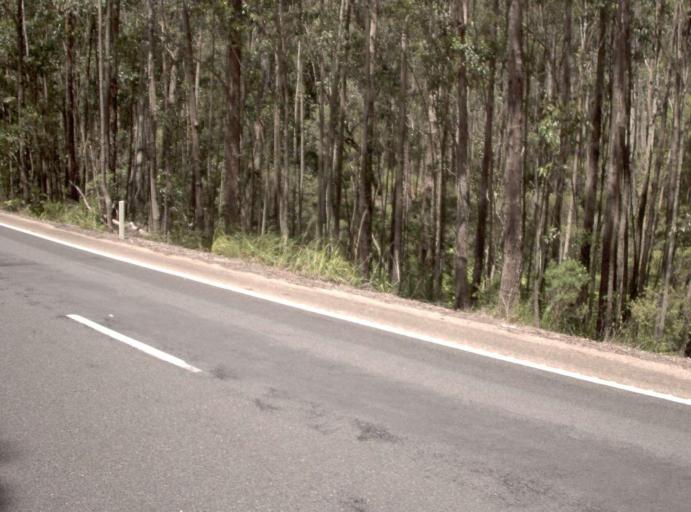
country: AU
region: New South Wales
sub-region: Bombala
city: Bombala
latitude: -37.6117
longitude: 148.8901
